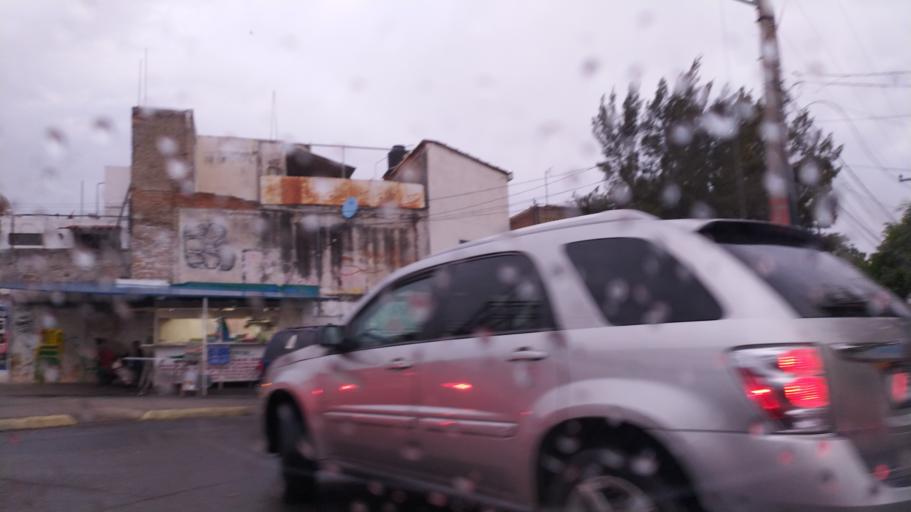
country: MX
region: Jalisco
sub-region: Zapopan
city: Zapopan
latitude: 20.7092
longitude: -103.3562
